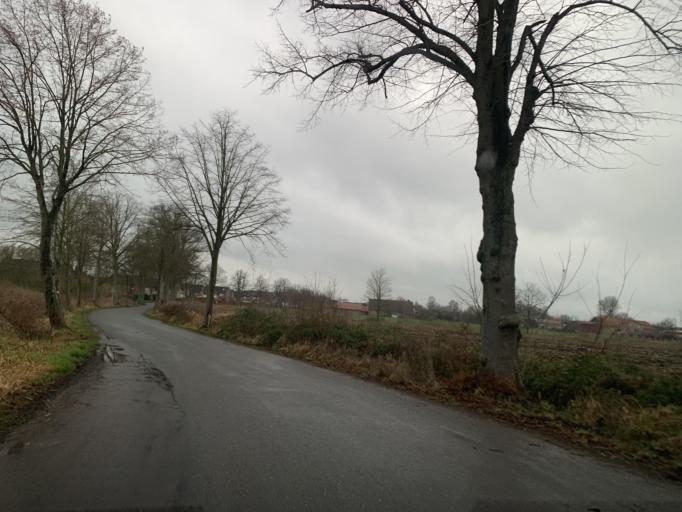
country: DE
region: North Rhine-Westphalia
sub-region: Regierungsbezirk Munster
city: Nordwalde
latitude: 52.0941
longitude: 7.4882
